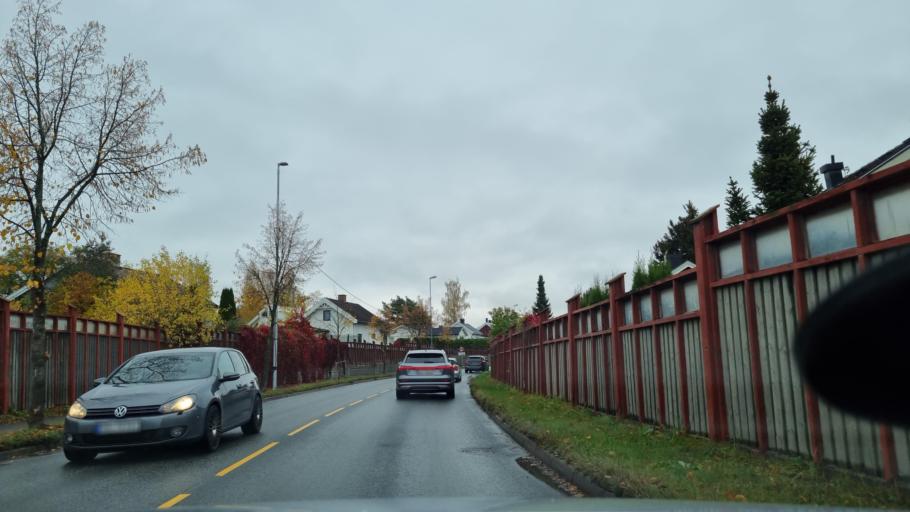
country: NO
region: Hedmark
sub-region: Hamar
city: Hamar
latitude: 60.8055
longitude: 11.0650
